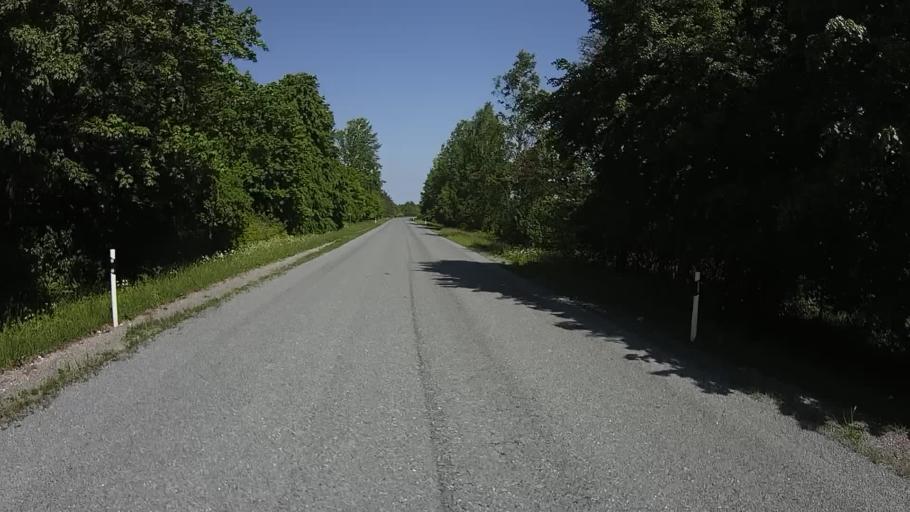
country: EE
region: Saare
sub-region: Kuressaare linn
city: Kuressaare
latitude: 58.0726
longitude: 22.2094
